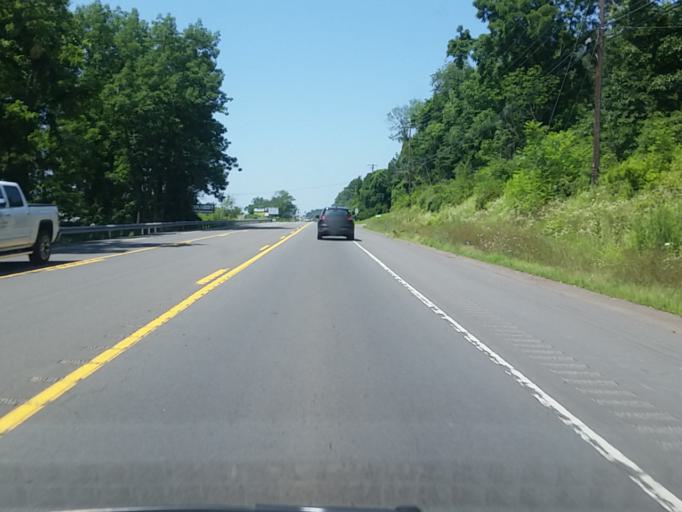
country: US
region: Pennsylvania
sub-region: Columbia County
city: Mifflinville
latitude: 41.0446
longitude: -76.2956
